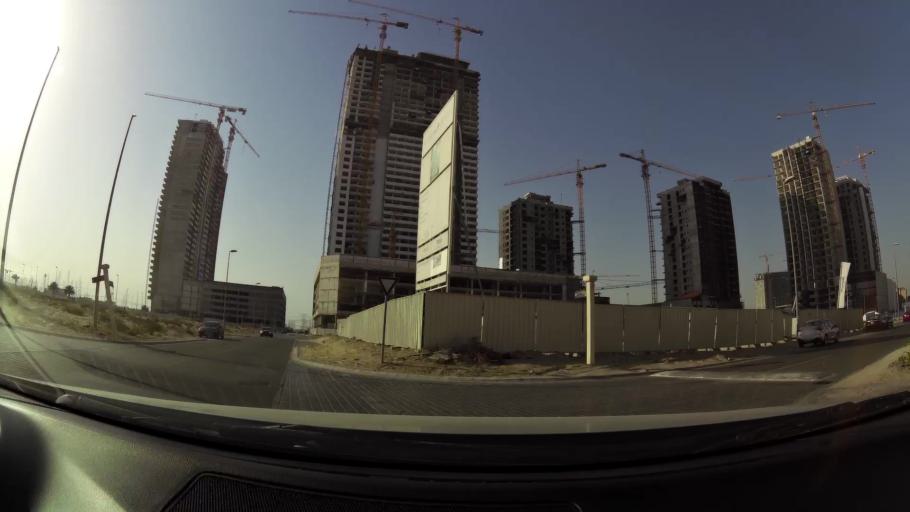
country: AE
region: Dubai
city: Dubai
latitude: 25.0512
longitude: 55.1994
